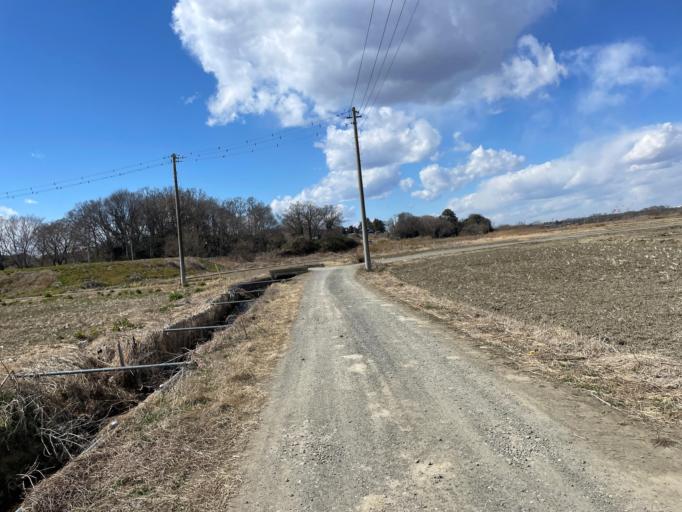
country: JP
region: Saitama
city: Sakado
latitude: 36.0108
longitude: 139.3938
